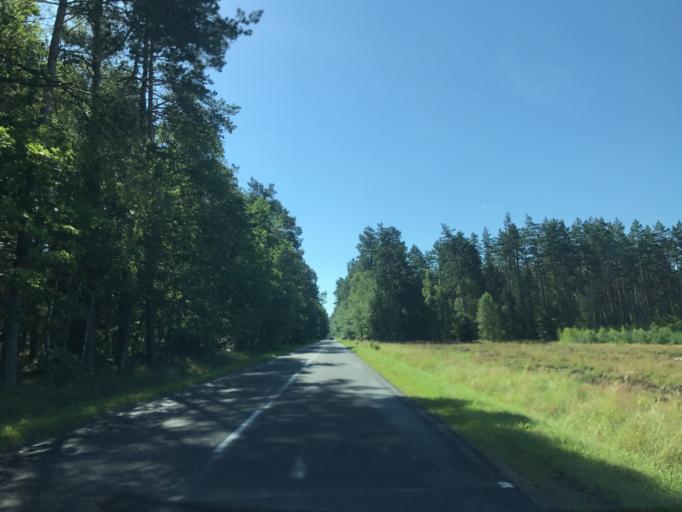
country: PL
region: Pomeranian Voivodeship
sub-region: Powiat bytowski
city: Czarna Dabrowka
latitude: 54.3890
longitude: 17.4770
